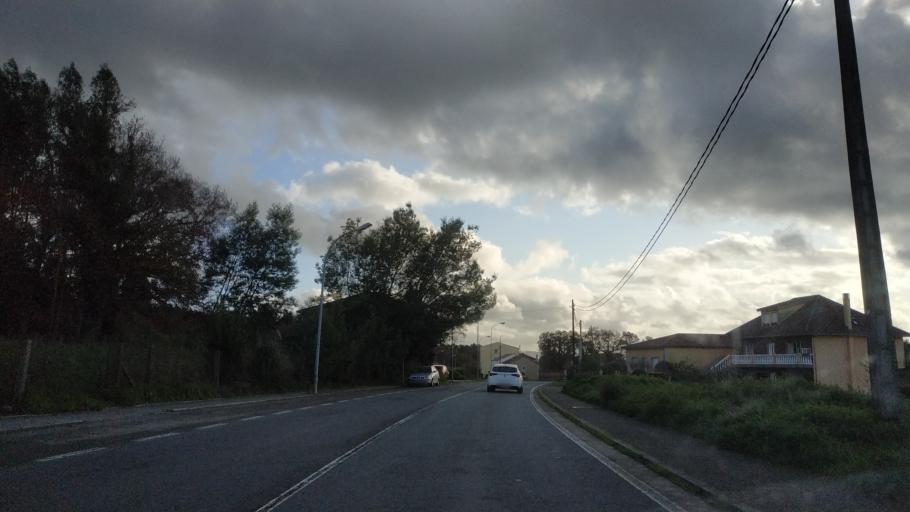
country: ES
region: Galicia
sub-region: Provincia da Coruna
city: Arzua
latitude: 42.9214
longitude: -8.1654
